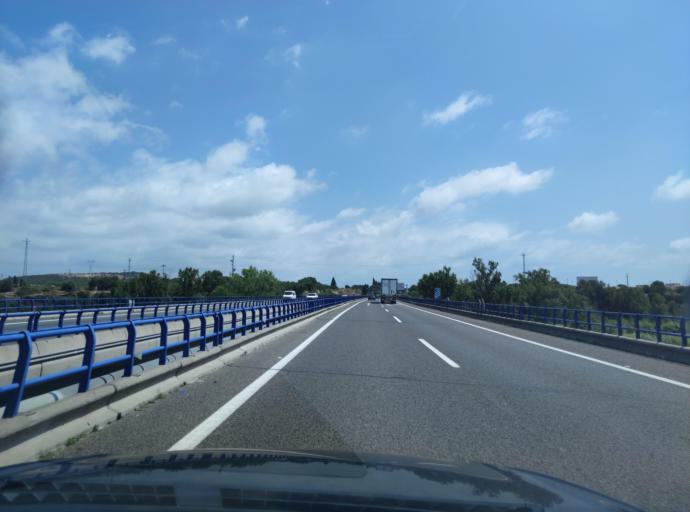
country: ES
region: Catalonia
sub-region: Provincia de Tarragona
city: Amposta
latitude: 40.7279
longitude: 0.5735
